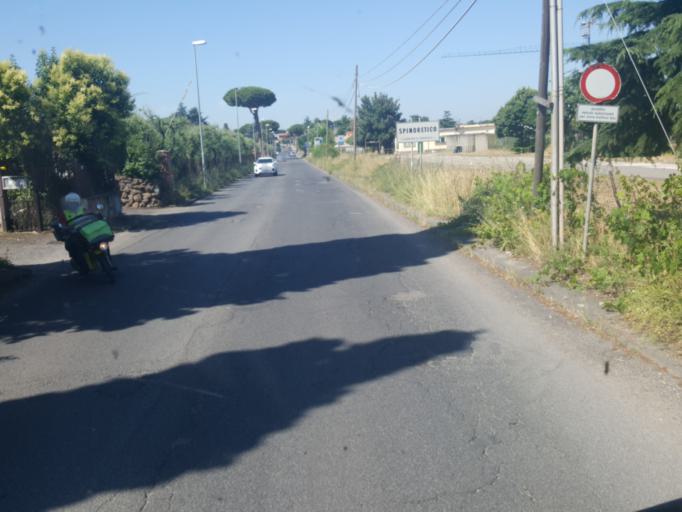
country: IT
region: Latium
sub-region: Citta metropolitana di Roma Capitale
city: Frascati
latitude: 41.8284
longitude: 12.6501
